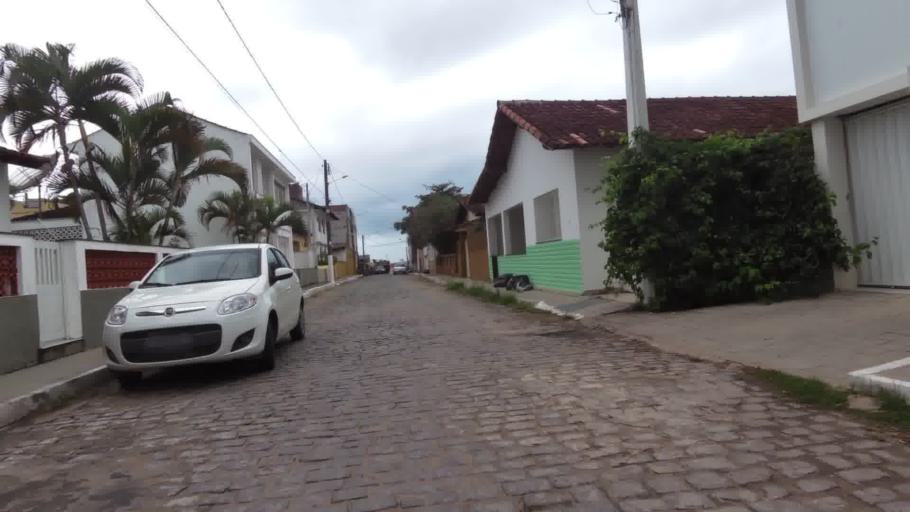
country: BR
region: Espirito Santo
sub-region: Marataizes
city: Marataizes
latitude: -21.0439
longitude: -40.8286
